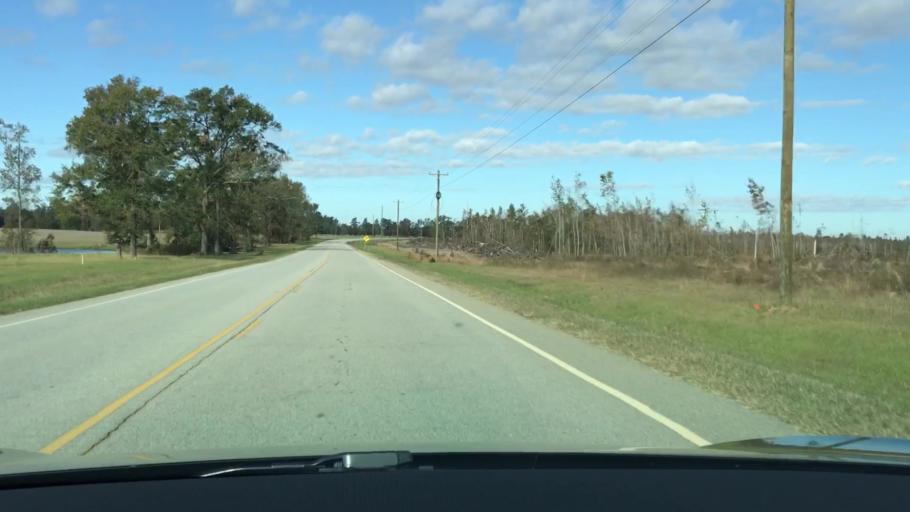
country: US
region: Georgia
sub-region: Jefferson County
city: Wrens
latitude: 33.1166
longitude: -82.4380
